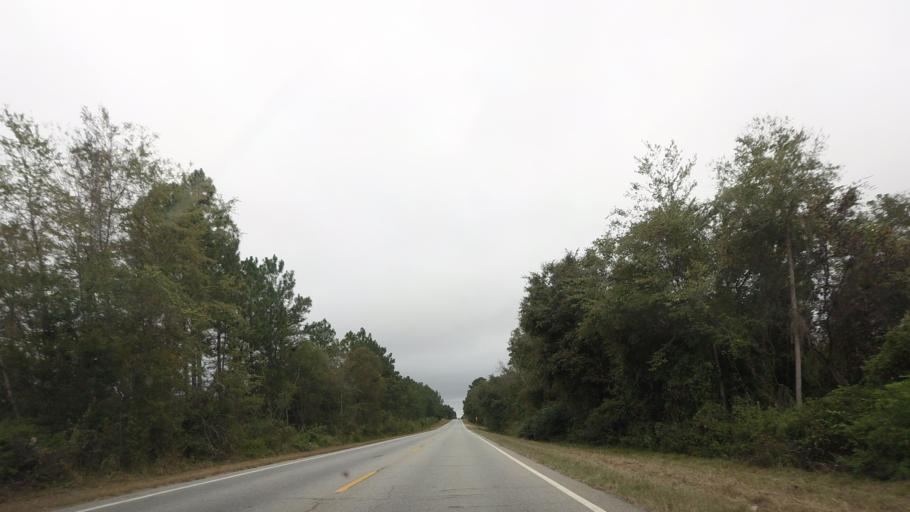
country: US
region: Georgia
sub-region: Berrien County
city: Ray City
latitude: 31.1056
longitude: -83.2091
